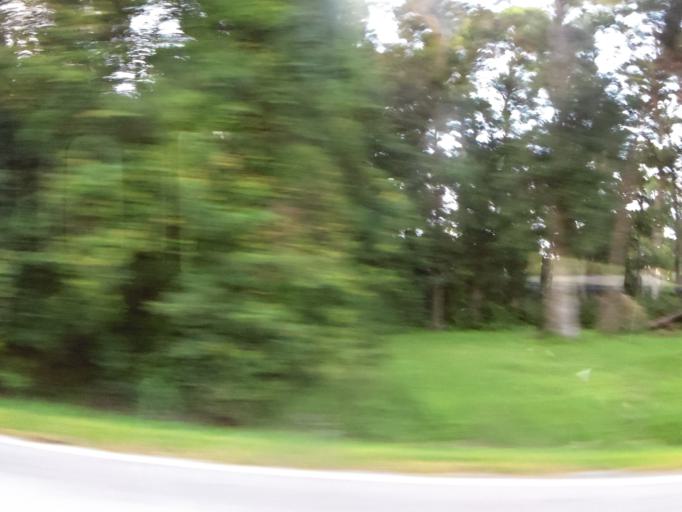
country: US
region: Florida
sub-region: Saint Johns County
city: Fruit Cove
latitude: 30.1903
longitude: -81.6292
